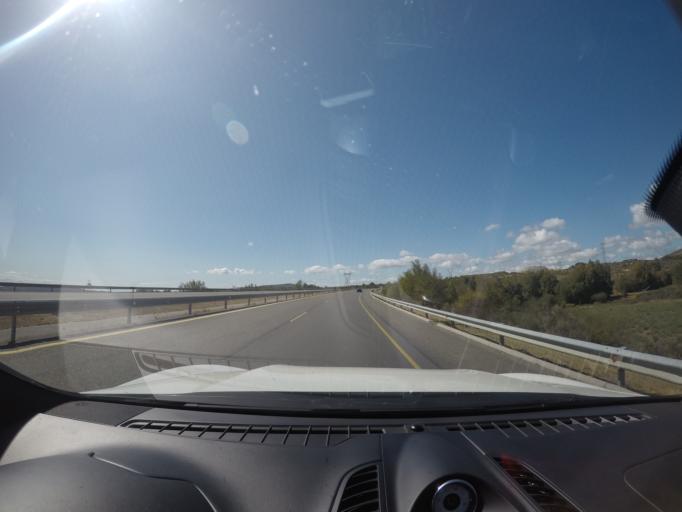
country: ES
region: Castille and Leon
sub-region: Provincia de Zamora
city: Pias
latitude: 42.0483
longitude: -7.0790
